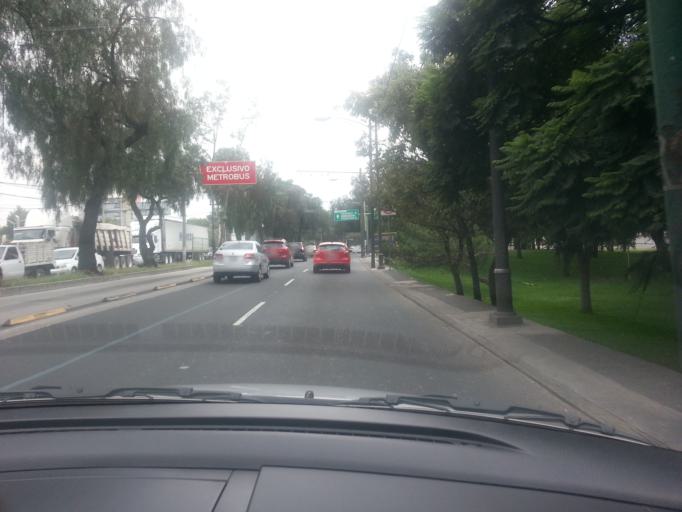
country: MX
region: Mexico City
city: Magdalena Contreras
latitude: 19.3363
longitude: -99.1901
